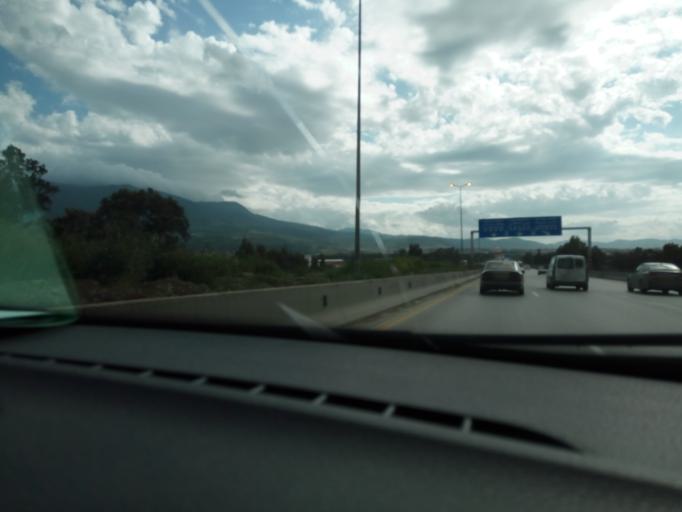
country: DZ
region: Blida
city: Chiffa
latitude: 36.4638
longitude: 2.7586
